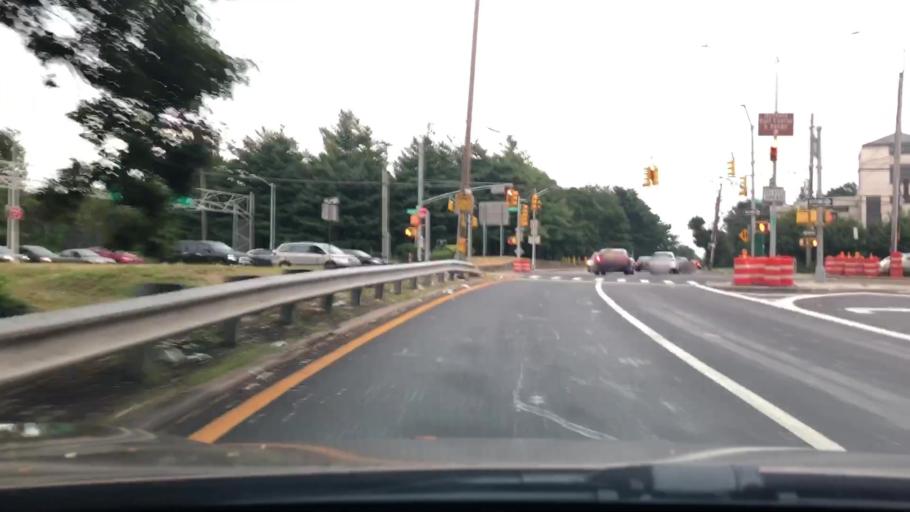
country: US
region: New York
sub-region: Westchester County
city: Yonkers
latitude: 40.8951
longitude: -73.8807
